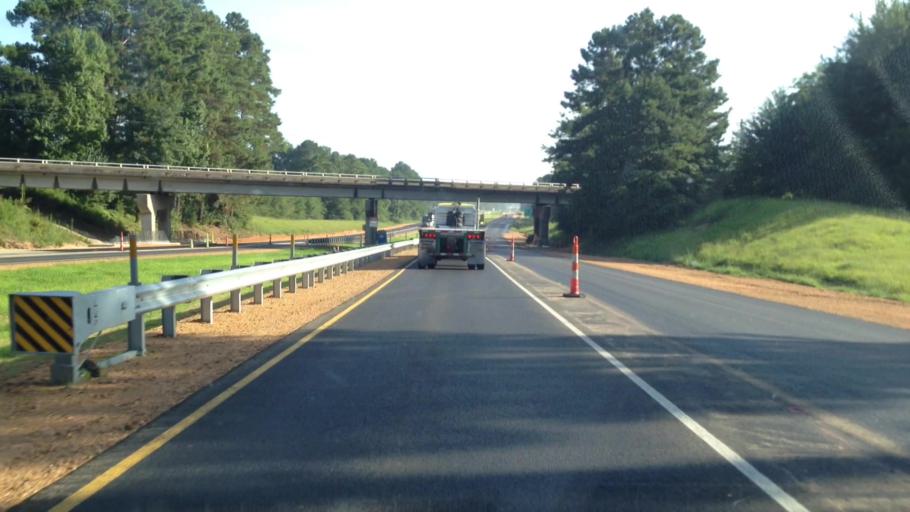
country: US
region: Mississippi
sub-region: Pike County
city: McComb
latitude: 31.2126
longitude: -90.4836
